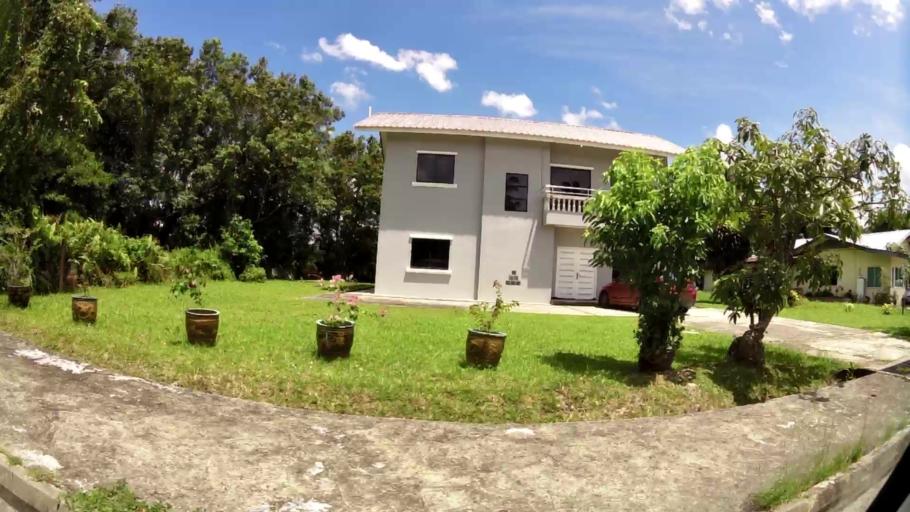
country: BN
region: Brunei and Muara
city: Bandar Seri Begawan
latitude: 4.9463
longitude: 114.9647
